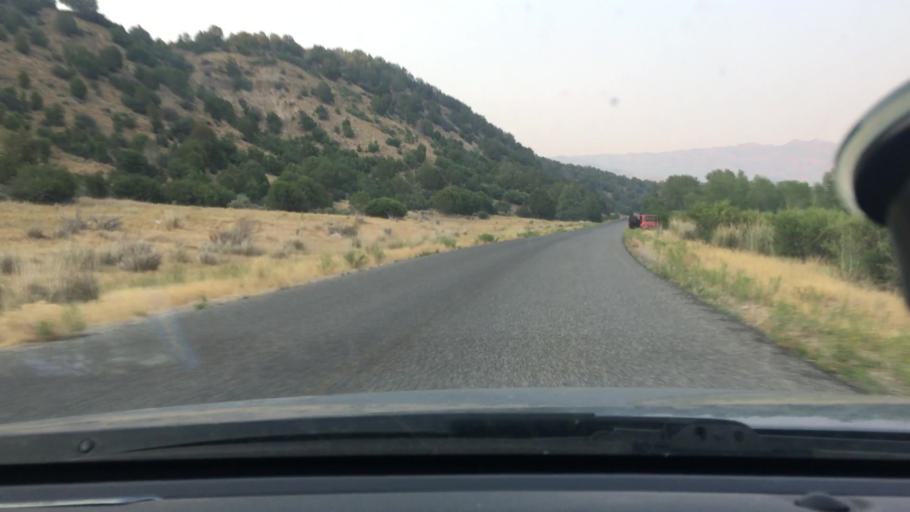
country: US
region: Utah
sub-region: Utah County
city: Mapleton
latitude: 40.0524
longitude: -111.4636
